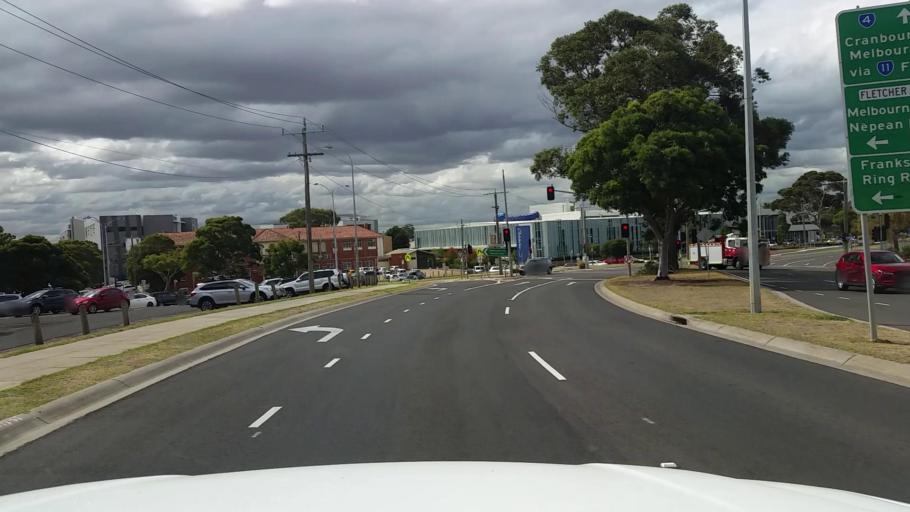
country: AU
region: Victoria
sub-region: Frankston
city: Frankston
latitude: -38.1460
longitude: 145.1256
